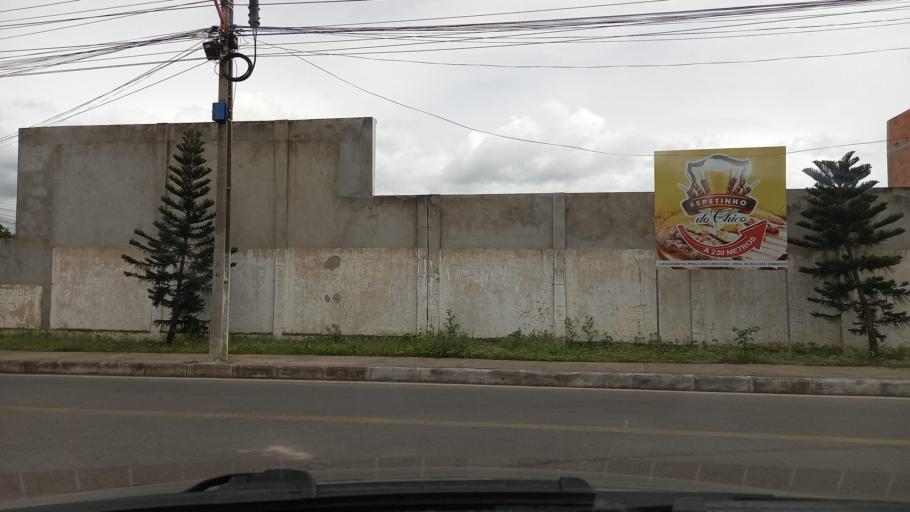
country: BR
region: Sergipe
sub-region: Caninde De Sao Francisco
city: Caninde de Sao Francisco
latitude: -9.6092
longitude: -37.7636
